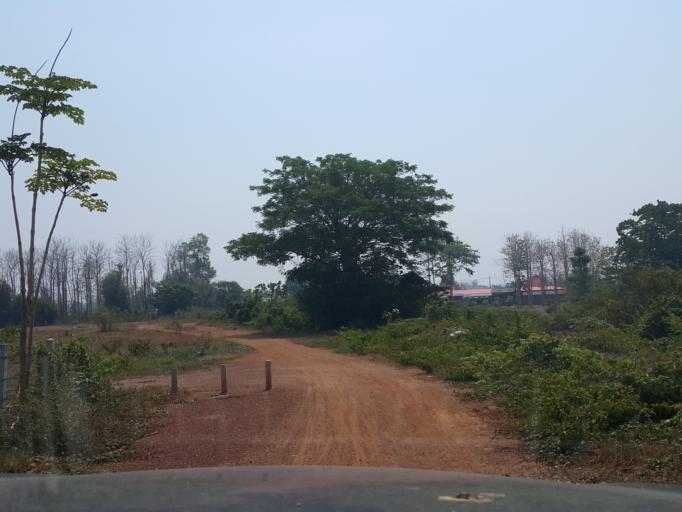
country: TH
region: Sukhothai
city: Thung Saliam
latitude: 17.3149
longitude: 99.5628
